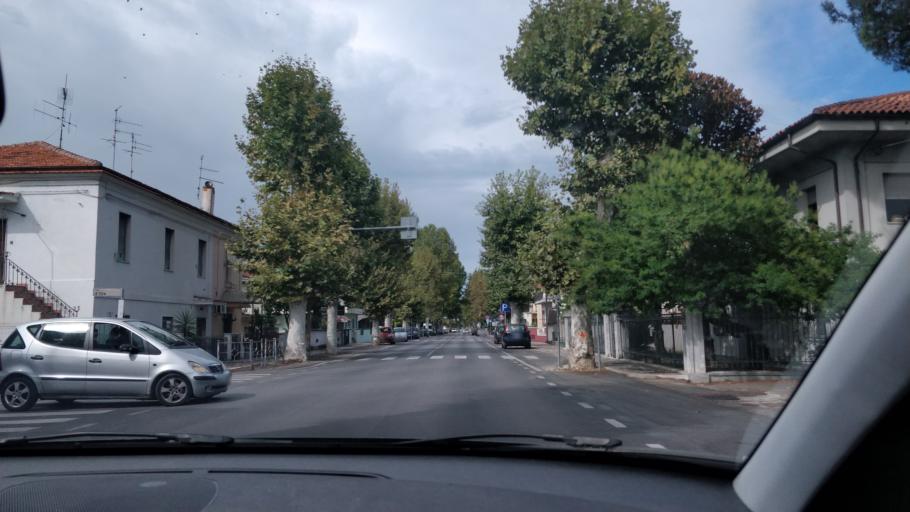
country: IT
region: Abruzzo
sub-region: Provincia di Chieti
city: Sambuceto
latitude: 42.4225
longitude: 14.1834
